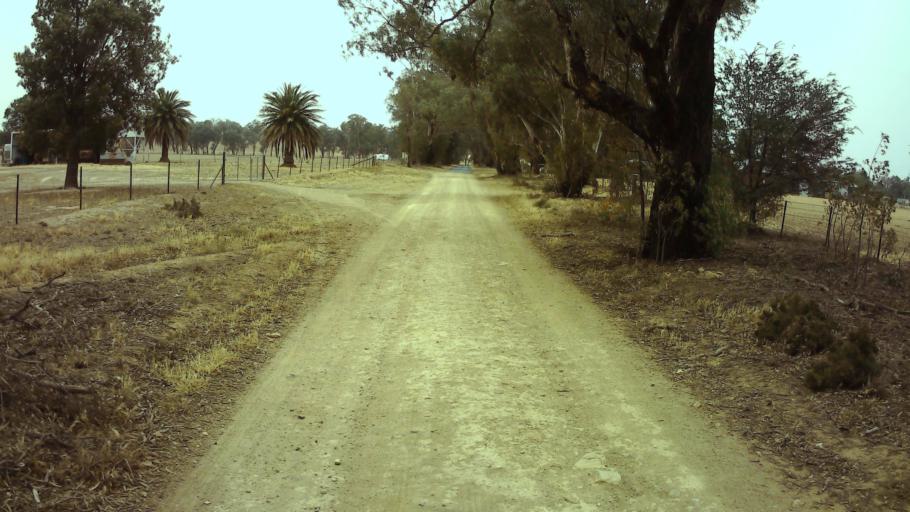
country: AU
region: New South Wales
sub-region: Weddin
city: Grenfell
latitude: -33.8997
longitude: 148.1426
